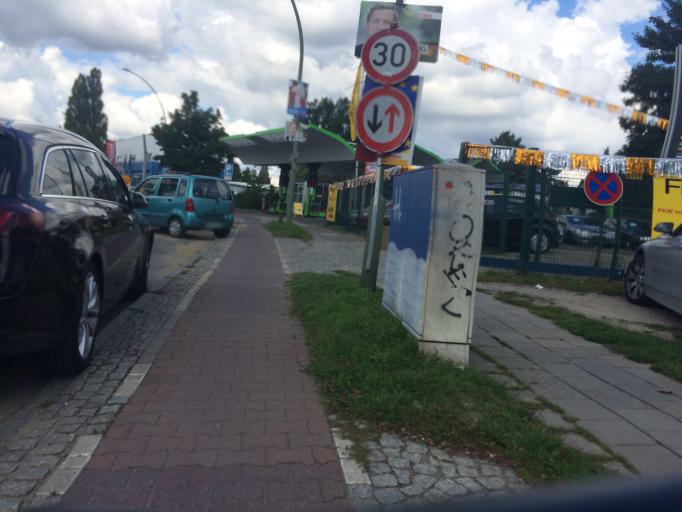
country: DE
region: Berlin
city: Heinersdorf
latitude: 52.5644
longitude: 13.4495
